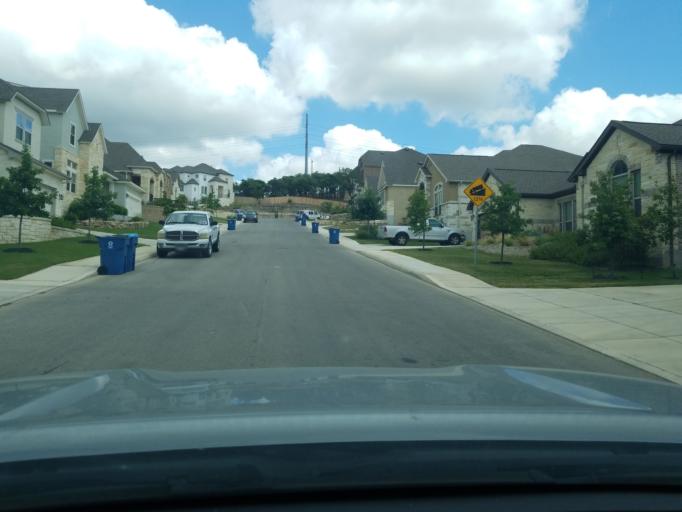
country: US
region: Texas
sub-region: Bexar County
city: Timberwood Park
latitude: 29.6654
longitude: -98.5126
